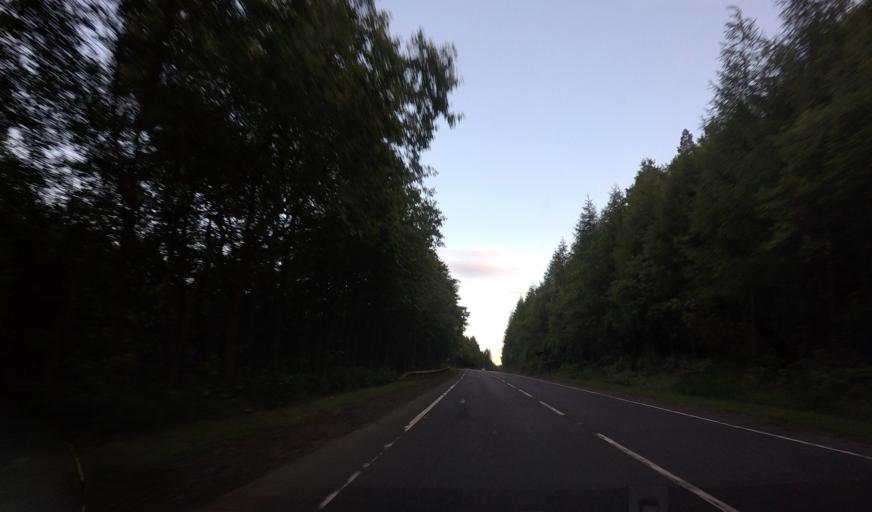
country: GB
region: Scotland
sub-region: Argyll and Bute
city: Garelochhead
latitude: 56.1833
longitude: -4.6933
